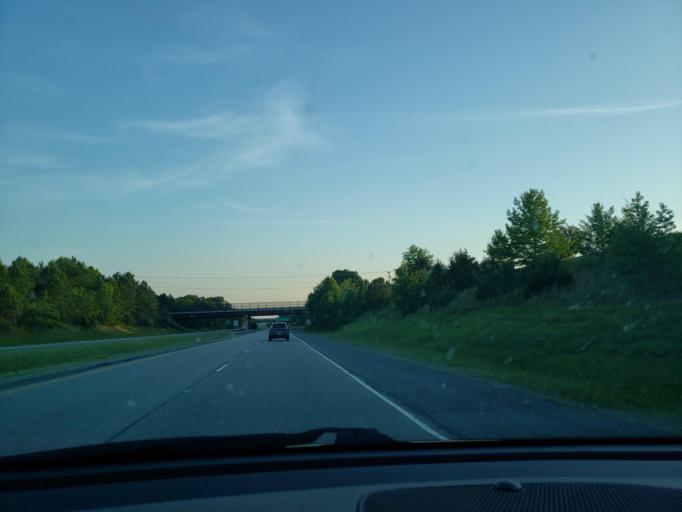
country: US
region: Virginia
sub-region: Henrico County
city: Fort Lee
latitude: 37.4628
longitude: -77.3771
